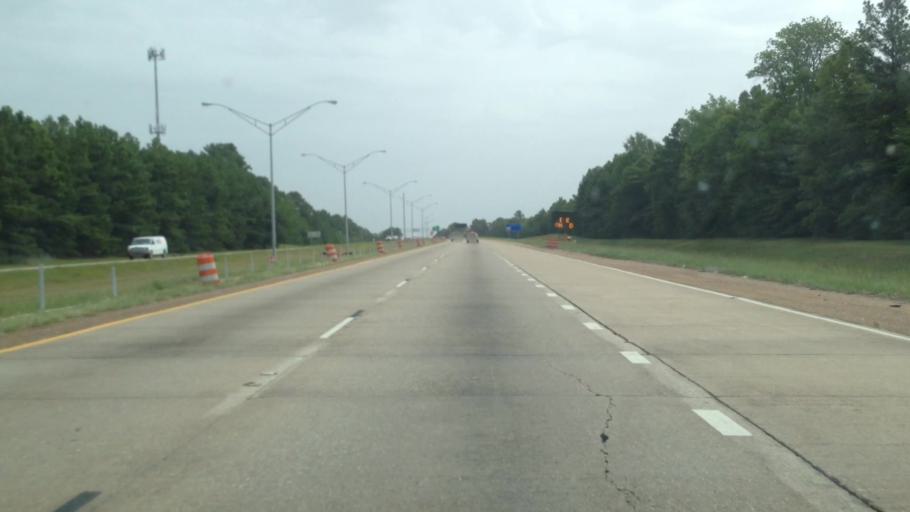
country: US
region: Louisiana
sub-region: Caddo Parish
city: Shreveport
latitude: 32.4891
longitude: -93.8255
